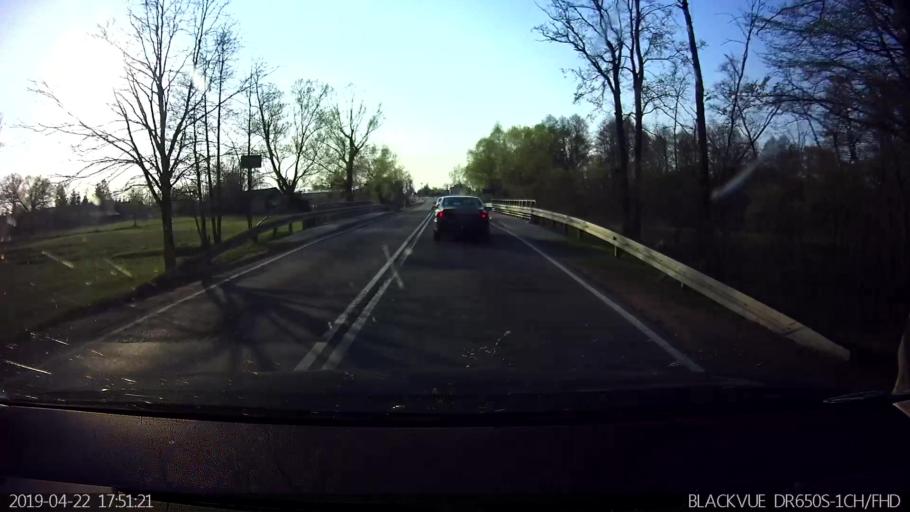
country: PL
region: Masovian Voivodeship
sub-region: Powiat wegrowski
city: Wegrow
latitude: 52.4346
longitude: 21.9945
